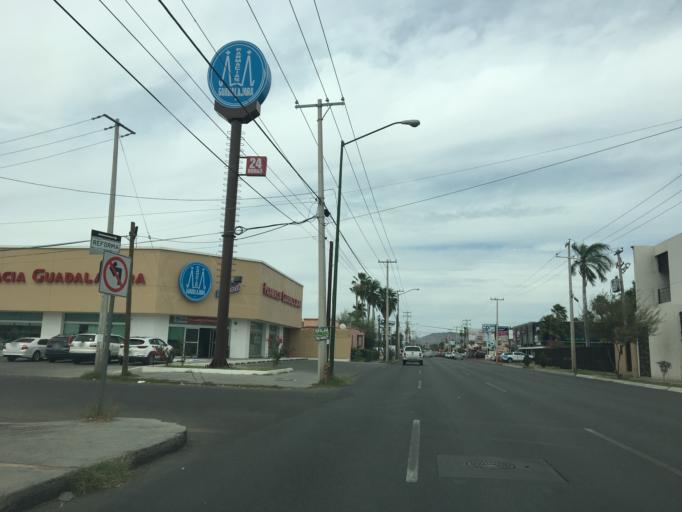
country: MX
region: Sonora
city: Hermosillo
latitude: 29.0753
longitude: -110.9655
